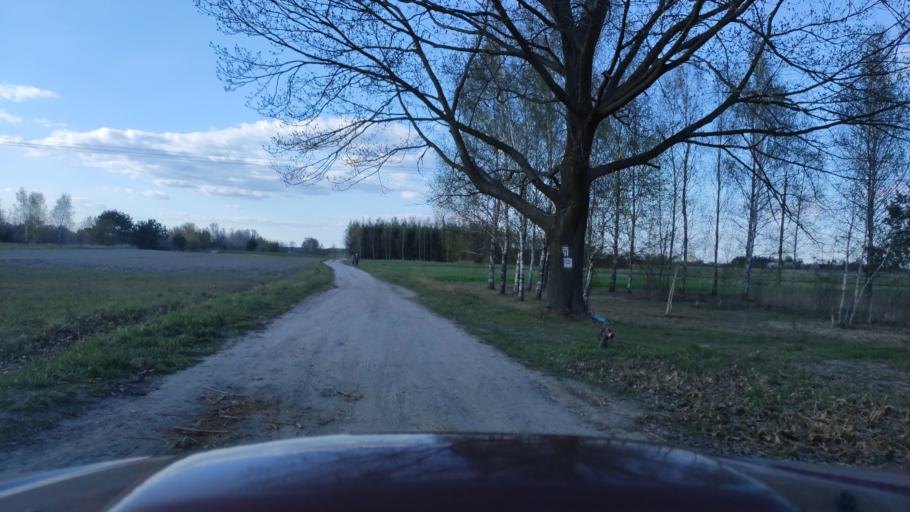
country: PL
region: Masovian Voivodeship
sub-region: Powiat zwolenski
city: Zwolen
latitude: 51.3661
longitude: 21.5755
